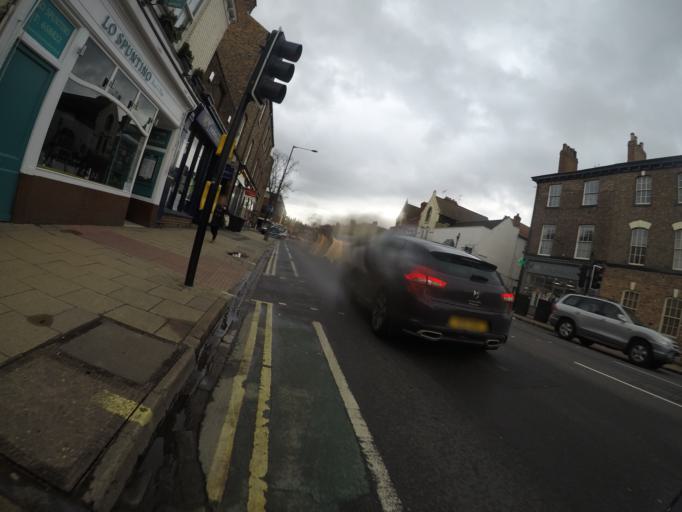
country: GB
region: England
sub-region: City of York
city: York
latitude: 53.9541
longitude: -1.0938
